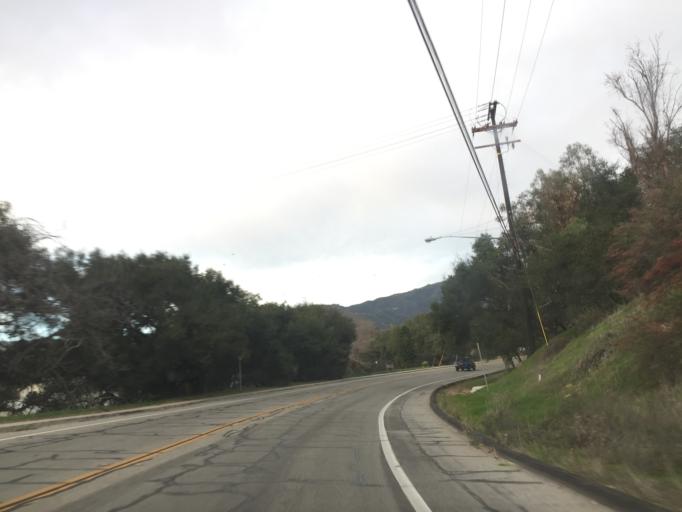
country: US
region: California
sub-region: Santa Barbara County
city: Goleta
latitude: 34.4485
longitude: -119.7917
